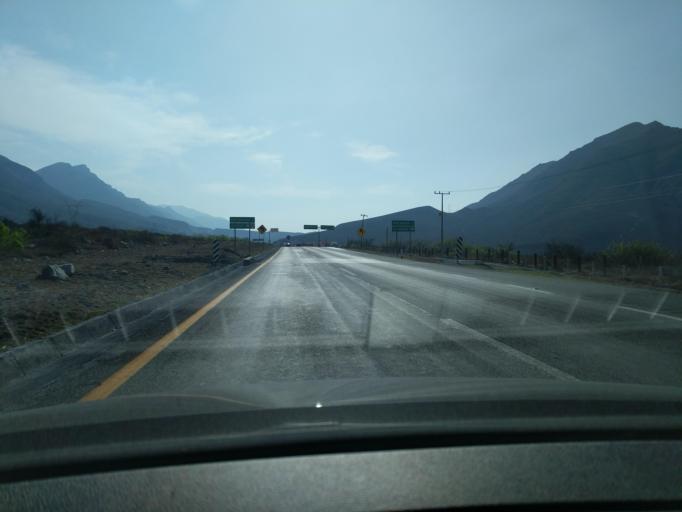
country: MX
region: Nuevo Leon
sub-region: Garcia
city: Las Torres de Guadalupe
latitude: 25.6618
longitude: -100.7112
